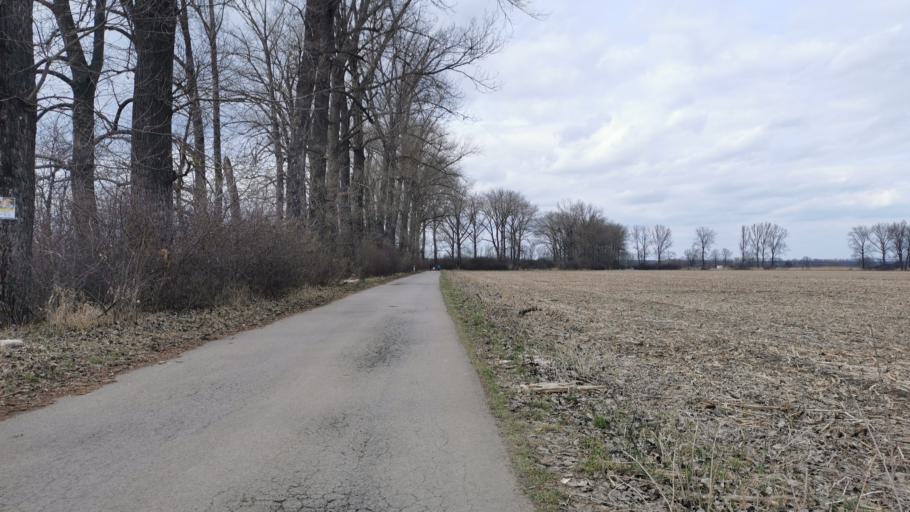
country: SK
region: Trnavsky
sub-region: Okres Skalica
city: Skalica
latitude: 48.8582
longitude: 17.2238
